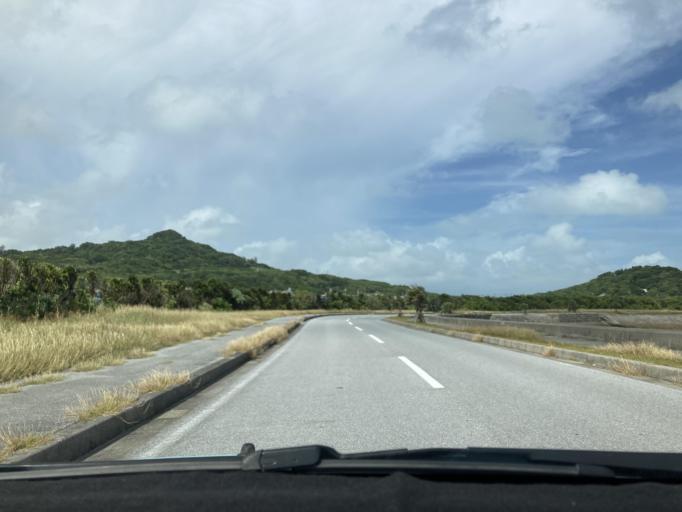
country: JP
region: Okinawa
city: Ginowan
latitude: 26.1816
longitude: 127.8216
